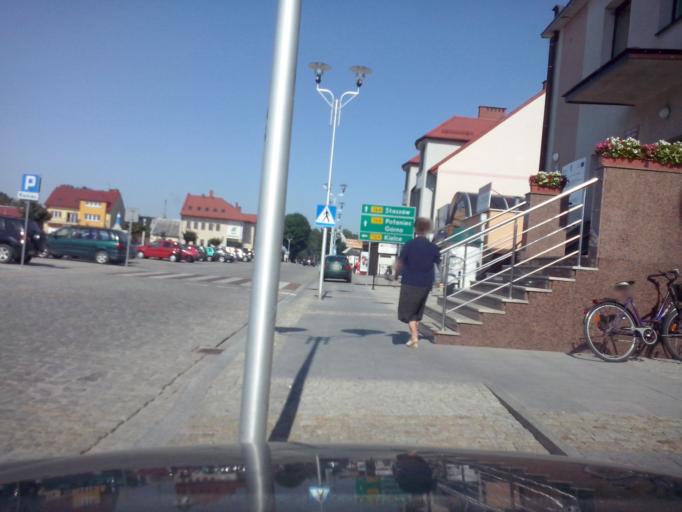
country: PL
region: Swietokrzyskie
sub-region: Powiat kielecki
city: Daleszyce
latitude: 50.8013
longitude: 20.8064
